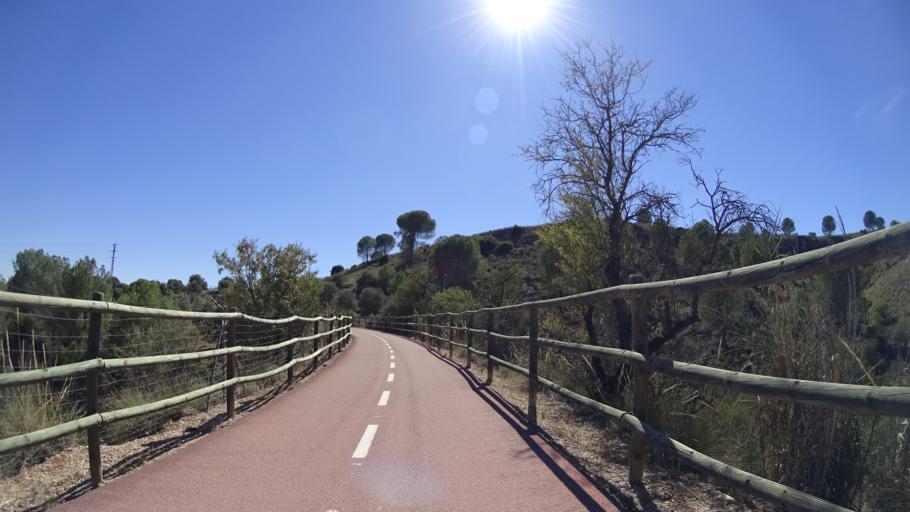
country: ES
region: Madrid
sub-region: Provincia de Madrid
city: Morata de Tajuna
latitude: 40.2312
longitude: -3.4658
